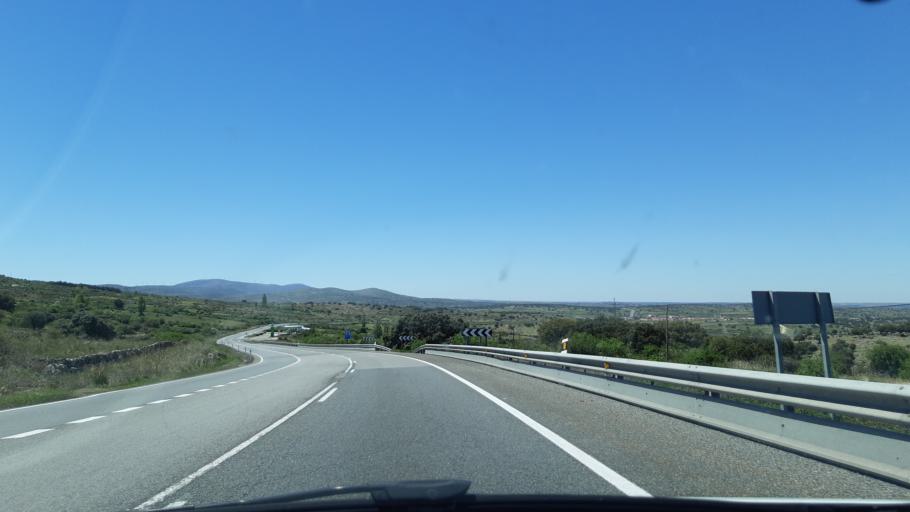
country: ES
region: Castille and Leon
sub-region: Provincia de Segovia
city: Vegas de Matute
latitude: 40.7502
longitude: -4.2916
